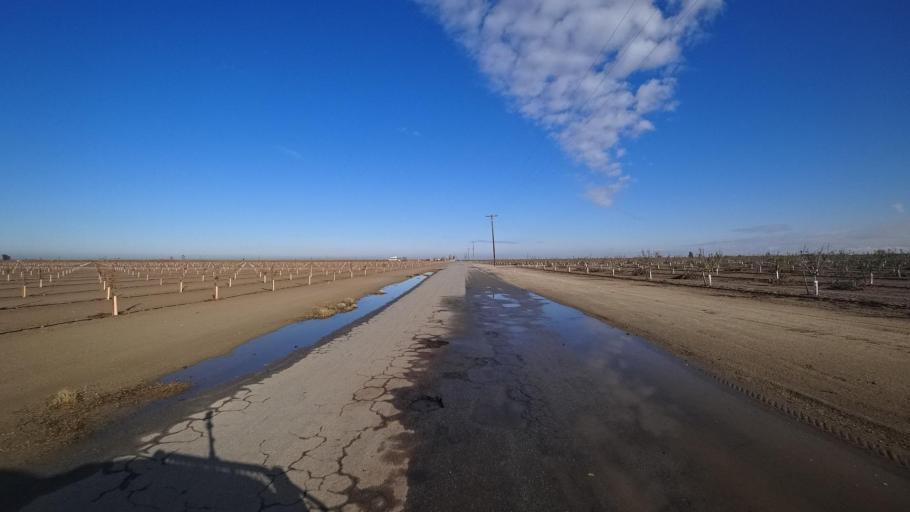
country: US
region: California
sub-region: Kern County
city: Delano
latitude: 35.7135
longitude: -119.3030
